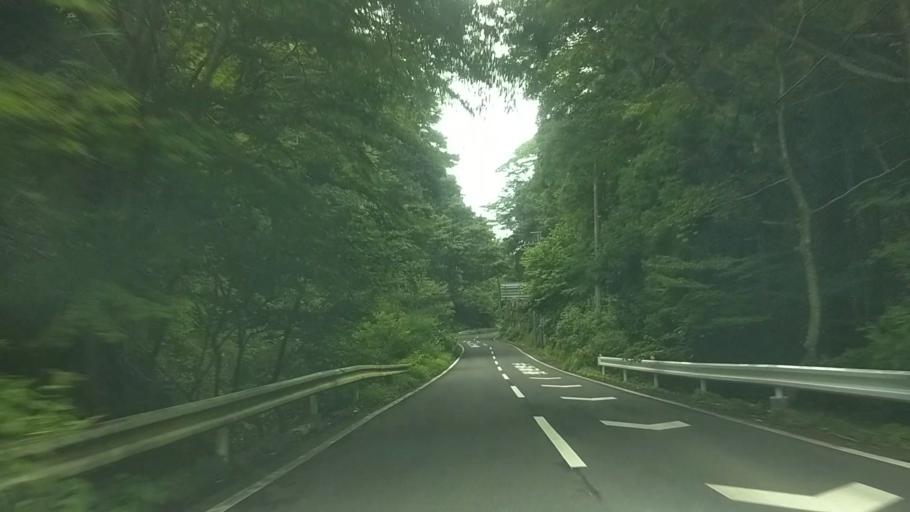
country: JP
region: Chiba
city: Kawaguchi
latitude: 35.2343
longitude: 140.0308
